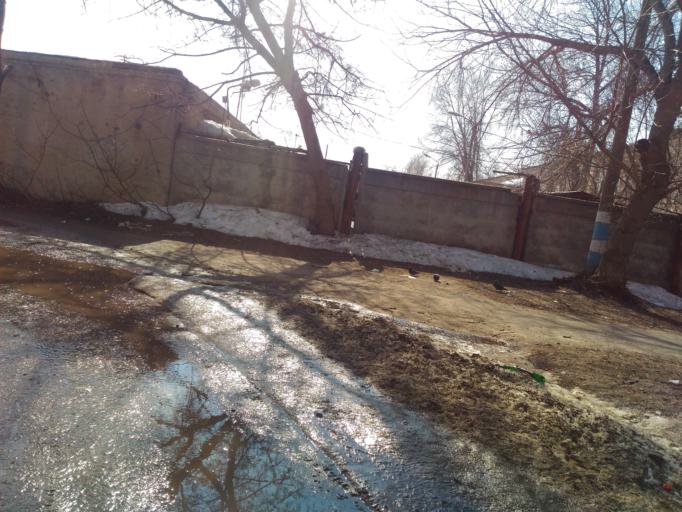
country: RU
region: Ulyanovsk
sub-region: Ulyanovskiy Rayon
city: Ulyanovsk
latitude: 54.3269
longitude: 48.4826
